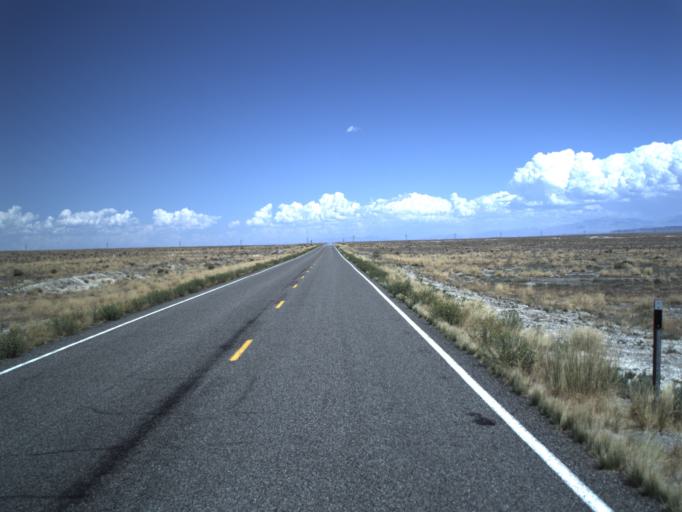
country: US
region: Utah
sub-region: Millard County
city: Delta
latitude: 39.1562
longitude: -113.0590
